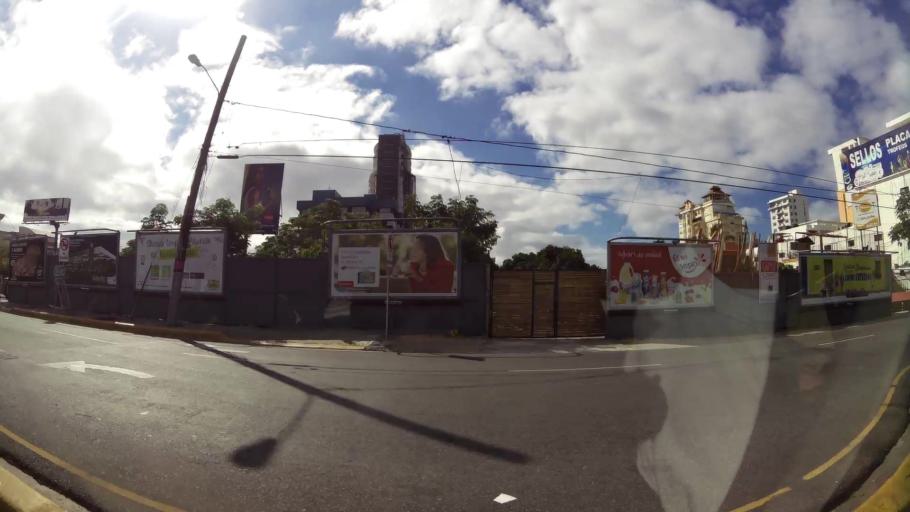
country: DO
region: Nacional
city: La Julia
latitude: 18.4603
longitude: -69.9343
